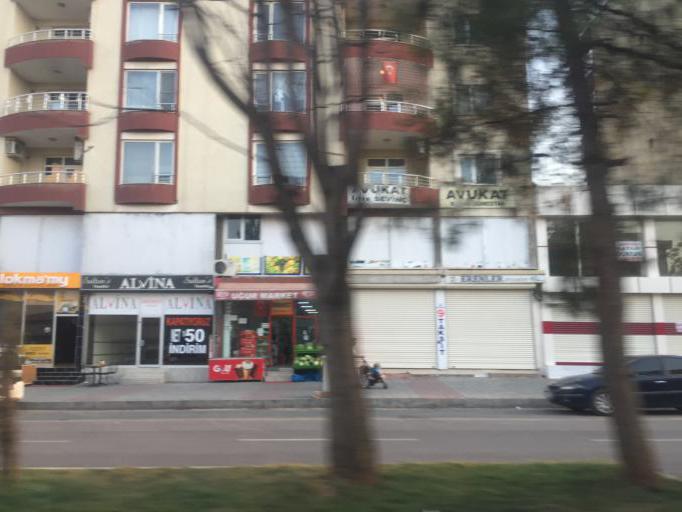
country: TR
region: Mardin
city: Midyat
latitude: 37.4241
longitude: 41.3420
